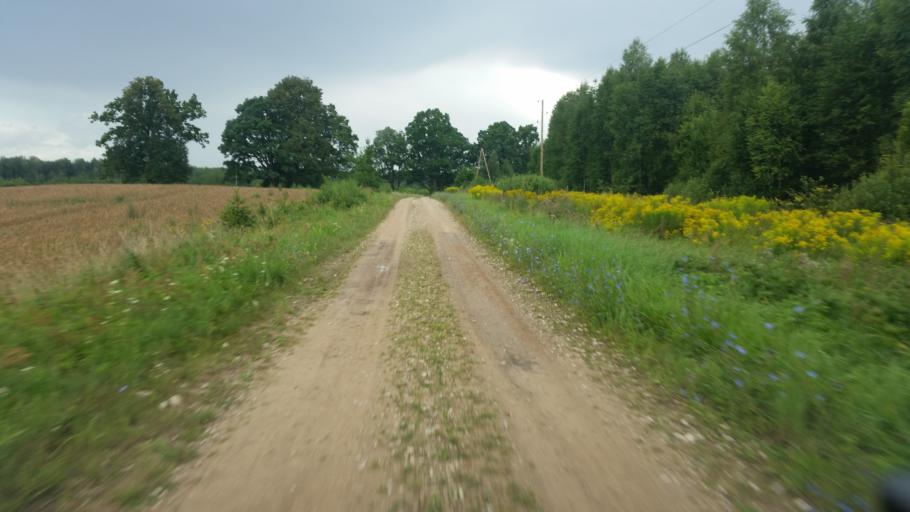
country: LV
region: Vecumnieki
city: Vecumnieki
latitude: 56.4630
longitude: 24.6665
